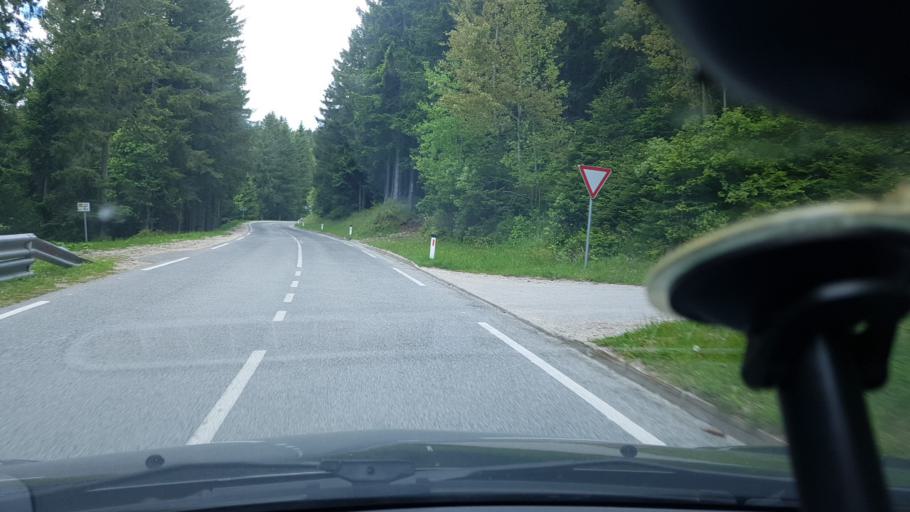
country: SI
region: Zrece
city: Zrece
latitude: 46.4478
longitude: 15.3446
